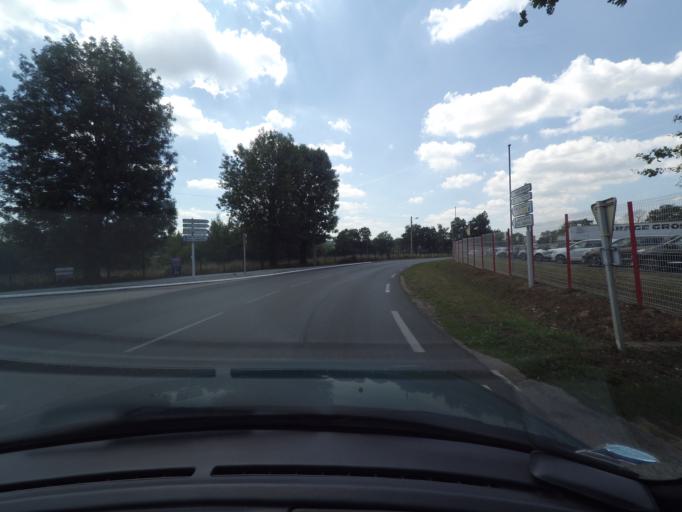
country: FR
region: Limousin
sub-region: Departement de la Haute-Vienne
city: Feytiat
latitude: 45.8147
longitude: 1.3081
